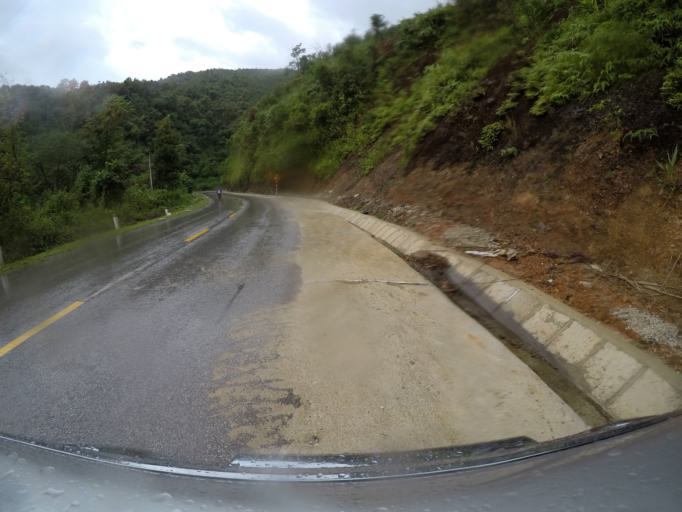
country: VN
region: Lai Chau
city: Than Uyen
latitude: 22.1258
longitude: 103.8098
